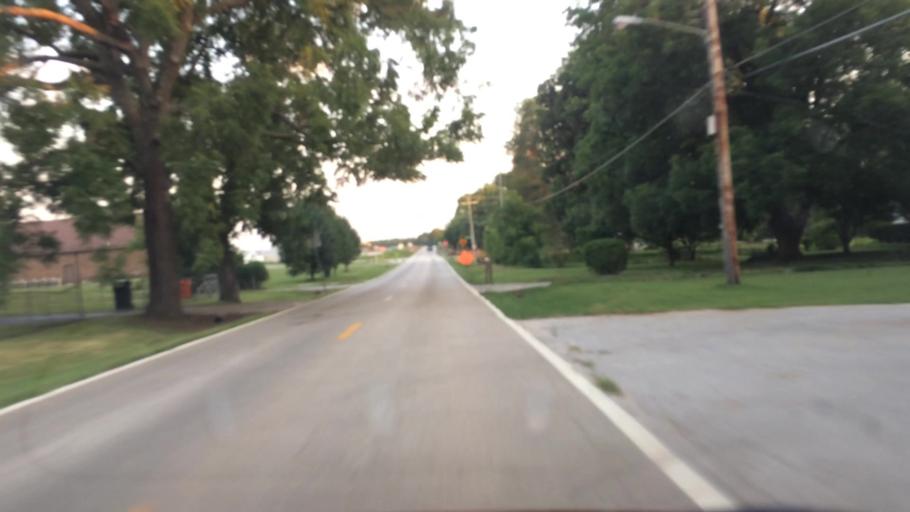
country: US
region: Missouri
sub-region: Greene County
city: Springfield
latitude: 37.2066
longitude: -93.3741
